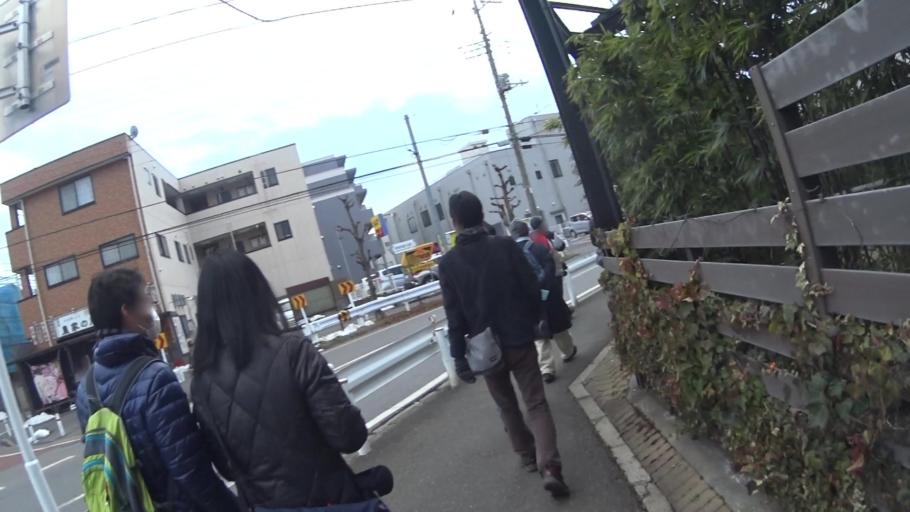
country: JP
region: Saitama
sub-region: Kawaguchi-shi
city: Hatogaya-honcho
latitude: 35.8659
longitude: 139.7049
